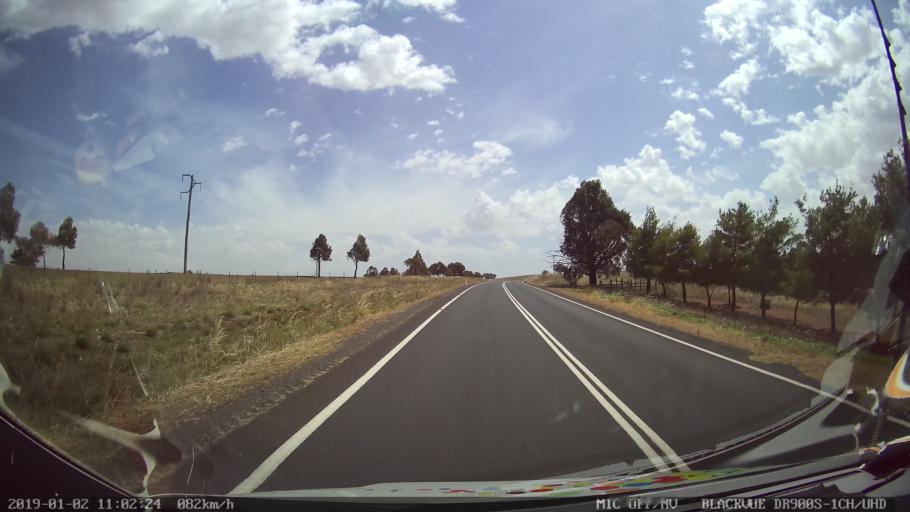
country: AU
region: New South Wales
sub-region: Young
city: Young
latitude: -34.5862
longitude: 148.3265
